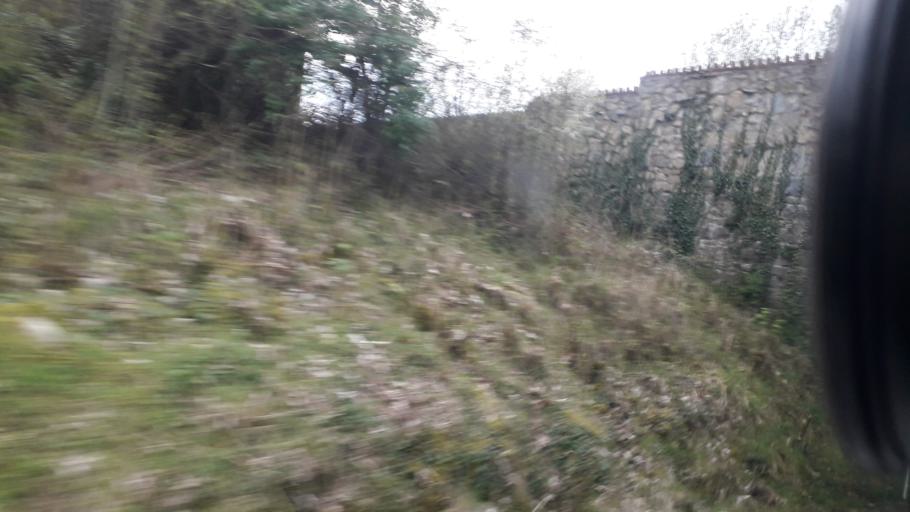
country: IE
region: Leinster
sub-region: An Longfort
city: Longford
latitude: 53.7254
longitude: -7.7732
